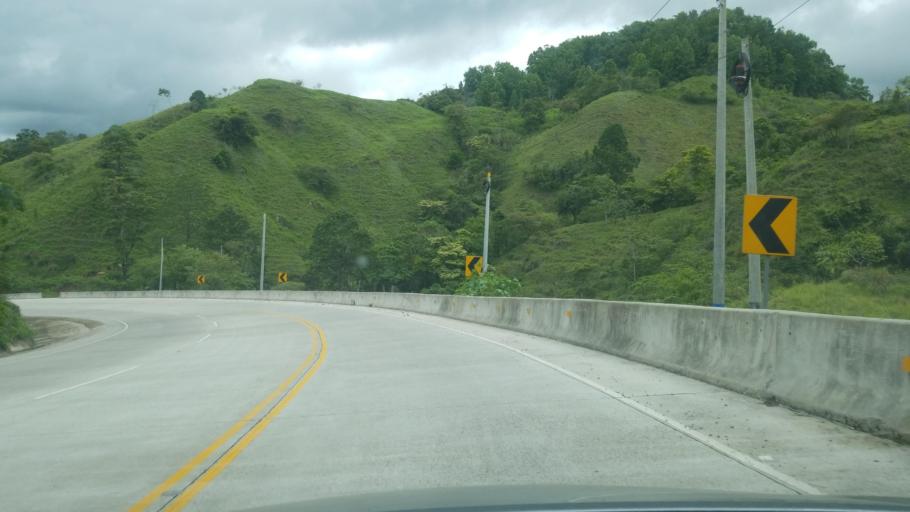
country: HN
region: Copan
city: San Jeronimo
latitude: 14.9667
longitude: -88.8942
